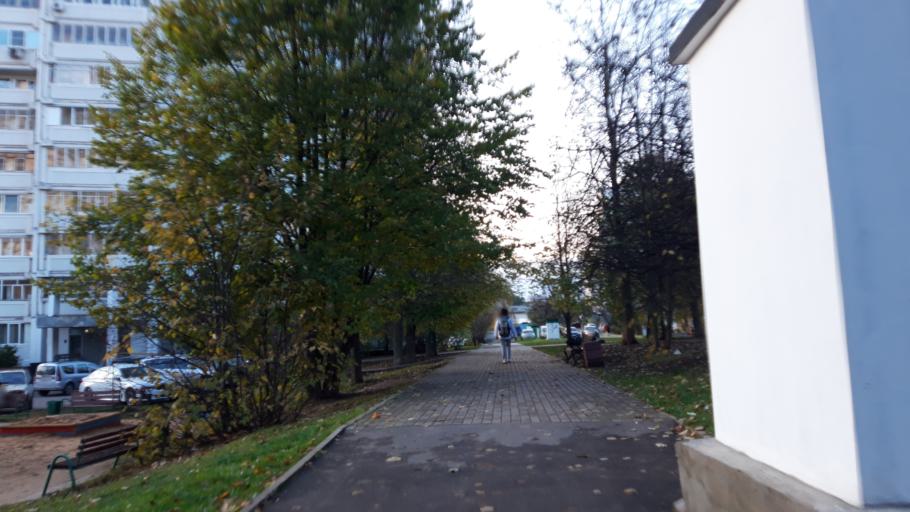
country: RU
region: Moscow
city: Zelenograd
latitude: 55.9936
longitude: 37.1934
